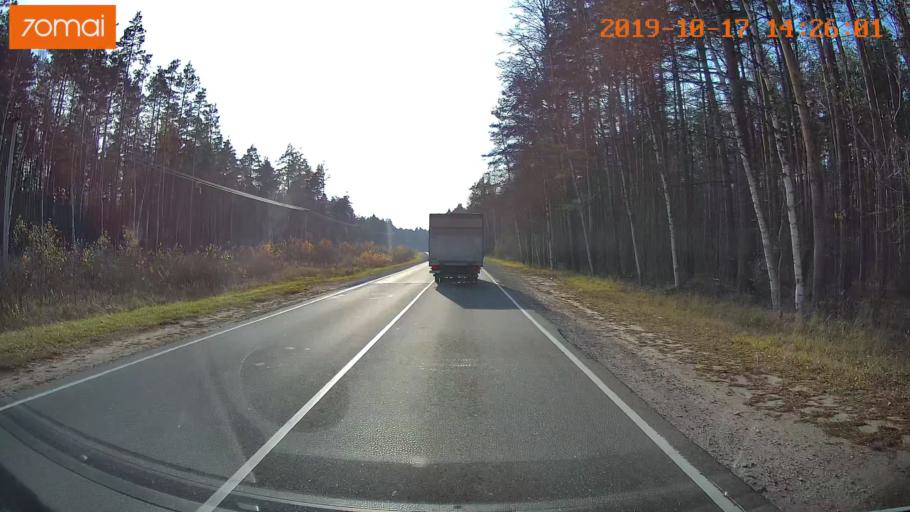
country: RU
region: Moskovskaya
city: Radovitskiy
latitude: 54.9954
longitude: 39.9724
